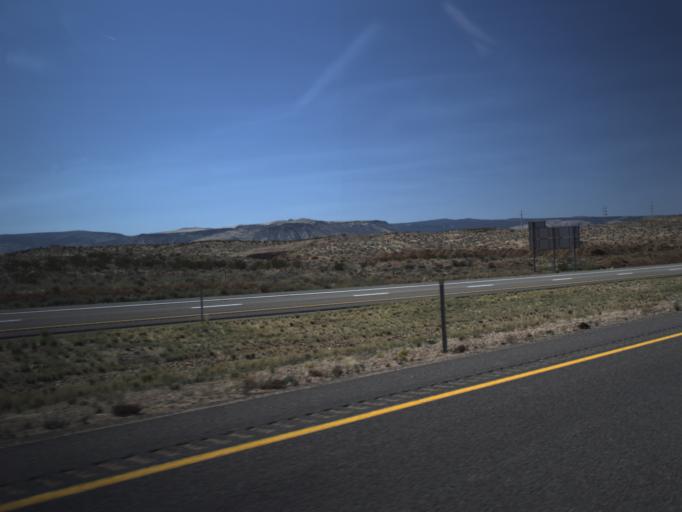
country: US
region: Utah
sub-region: Washington County
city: Saint George
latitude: 37.0051
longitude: -113.5262
